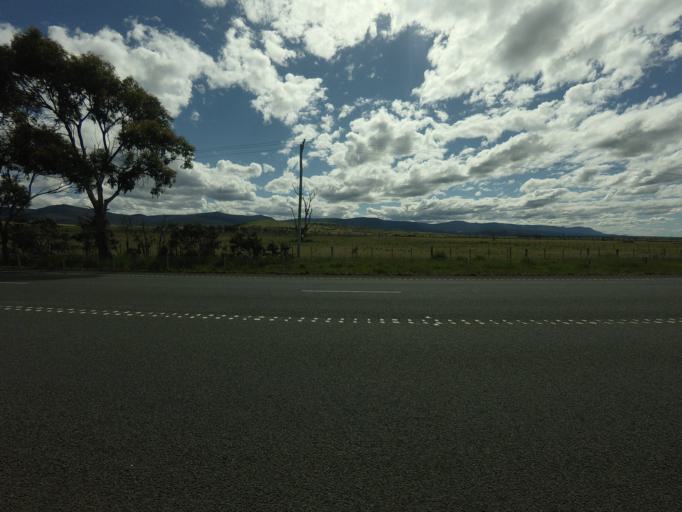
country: AU
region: Tasmania
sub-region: Brighton
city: Bridgewater
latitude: -42.1614
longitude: 147.4008
